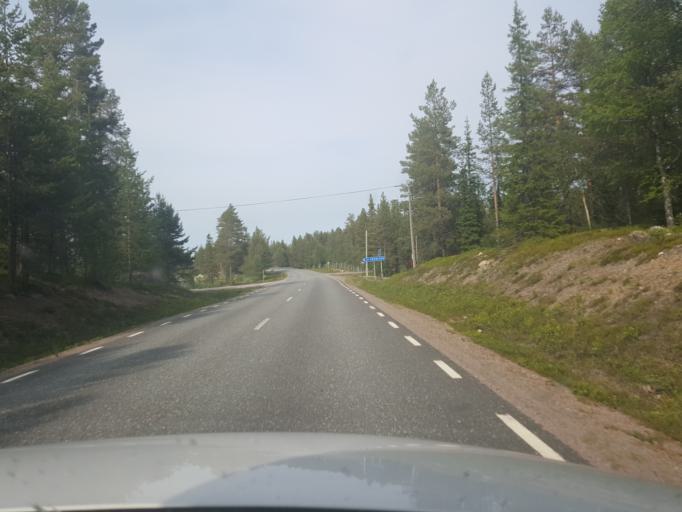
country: SE
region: Norrbotten
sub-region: Arjeplogs Kommun
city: Arjeplog
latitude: 65.8333
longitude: 18.0205
